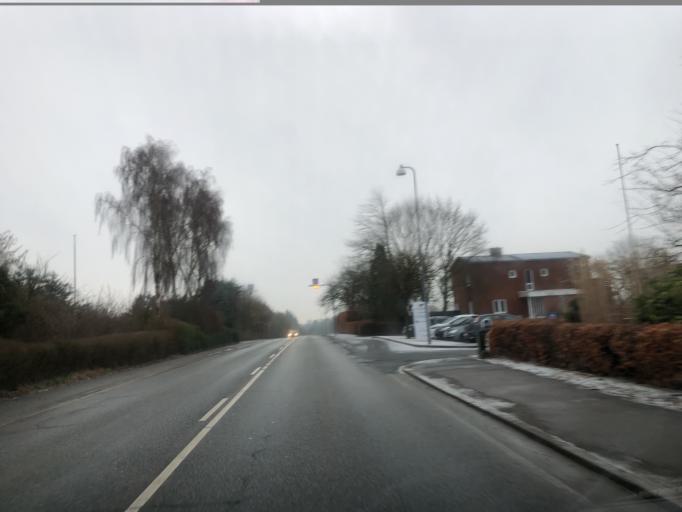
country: DK
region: South Denmark
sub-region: Vejle Kommune
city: Jelling
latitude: 55.8147
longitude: 9.3503
